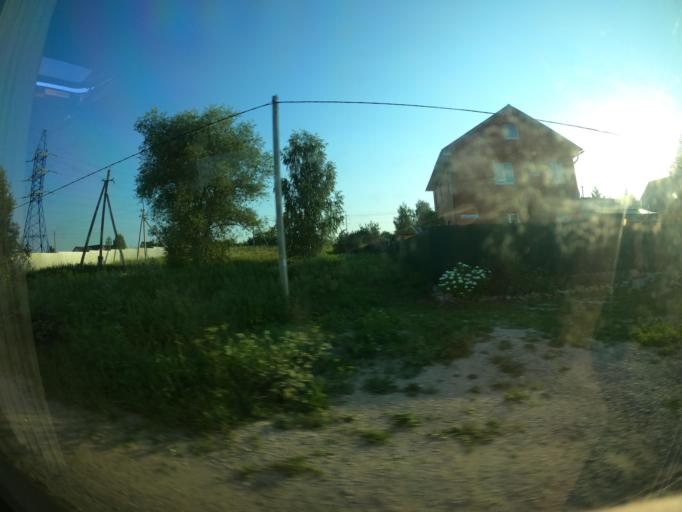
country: RU
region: Moskovskaya
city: Serpukhov
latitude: 54.9433
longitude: 37.3506
